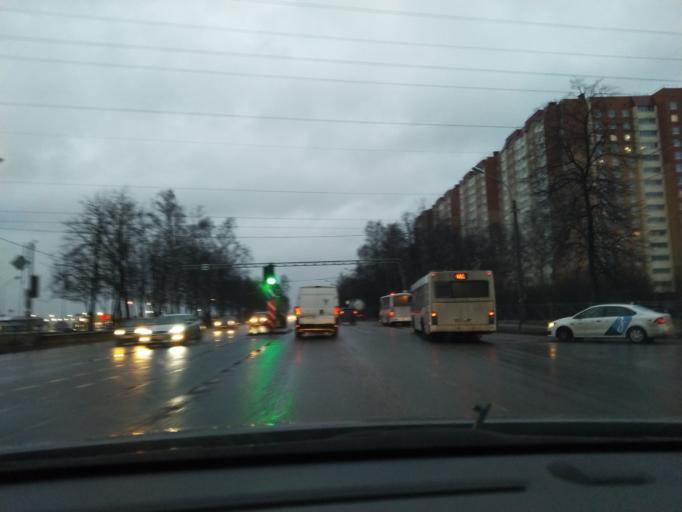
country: RU
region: St.-Petersburg
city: Gorelovo
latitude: 59.7910
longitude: 30.1462
